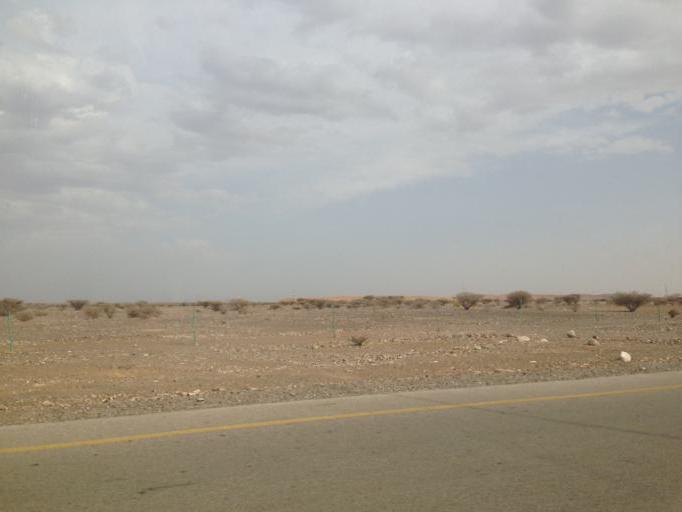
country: OM
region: Ash Sharqiyah
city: Badiyah
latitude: 22.5042
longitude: 58.9465
